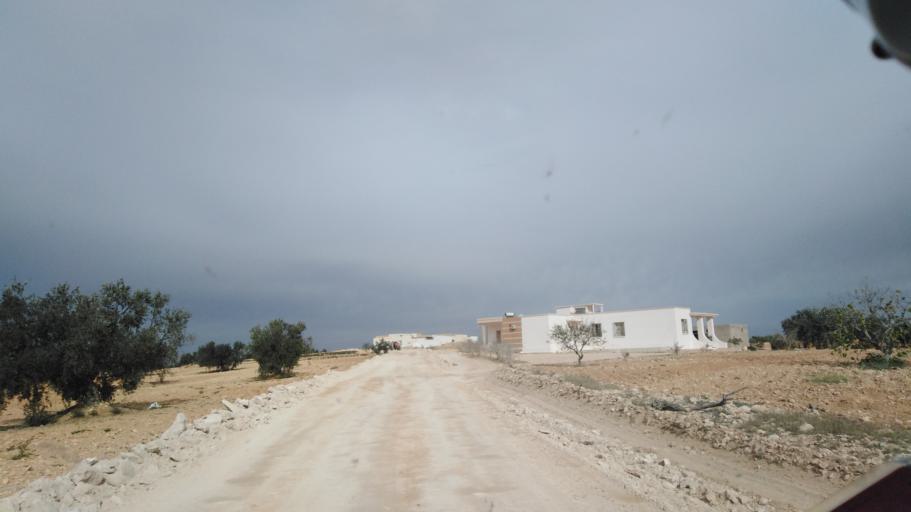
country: TN
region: Safaqis
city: Bi'r `Ali Bin Khalifah
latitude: 34.8135
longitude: 10.3076
